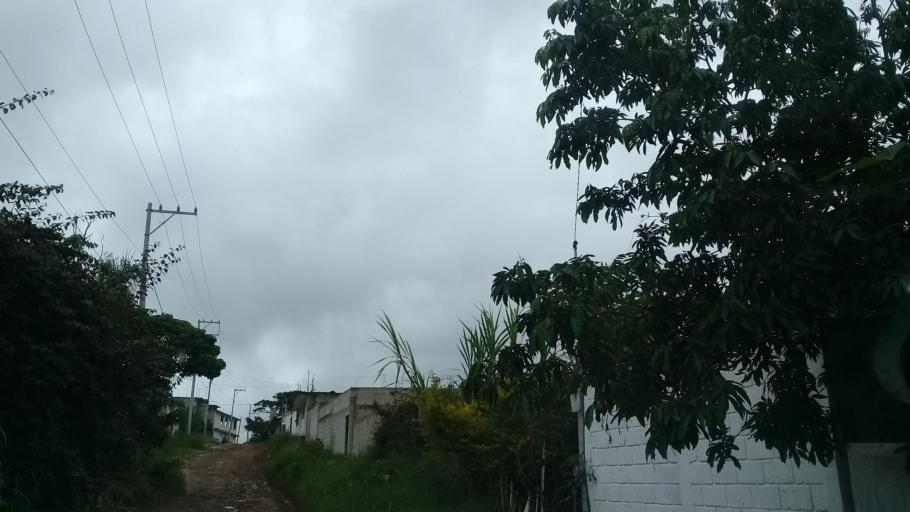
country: MX
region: Veracruz
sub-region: Emiliano Zapata
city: Las Trancas
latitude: 19.4958
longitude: -96.8655
